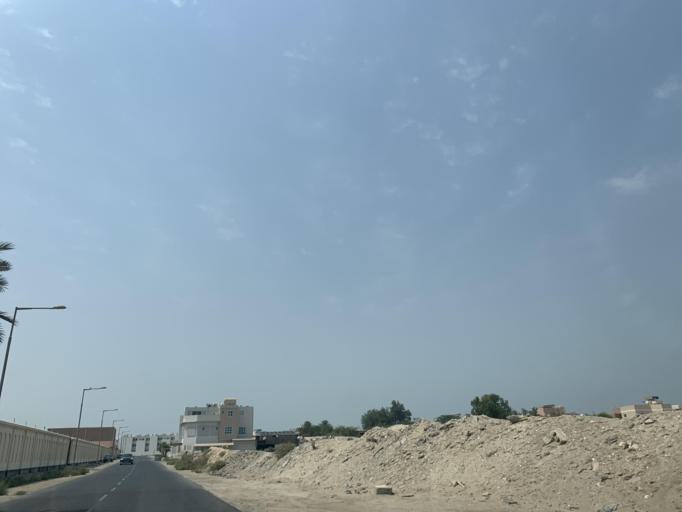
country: BH
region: Manama
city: Jidd Hafs
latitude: 26.2072
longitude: 50.4869
